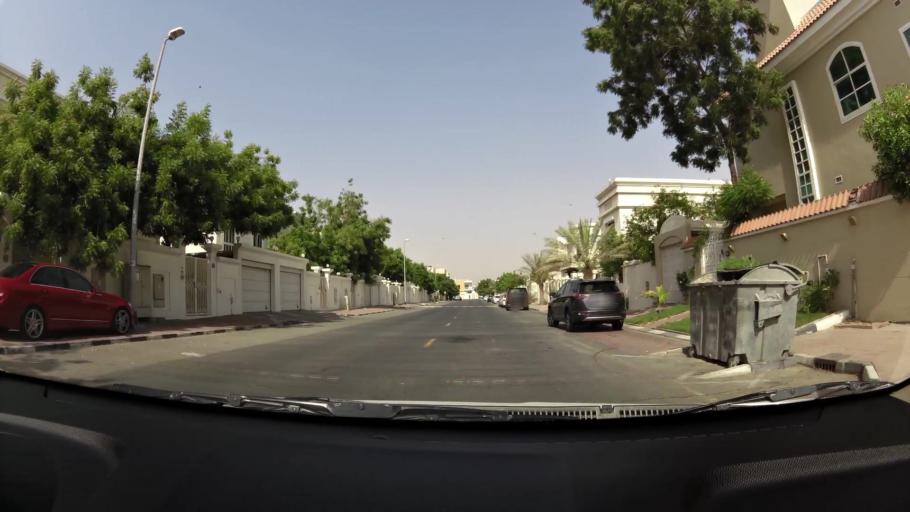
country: AE
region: Ash Shariqah
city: Sharjah
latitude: 25.2383
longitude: 55.3531
